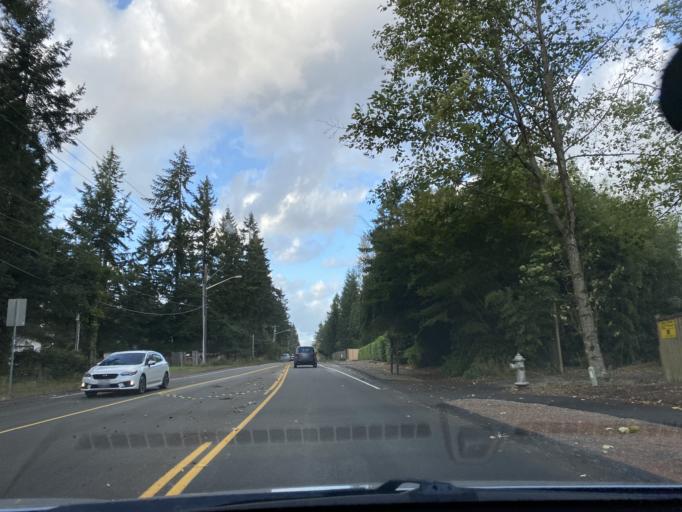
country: US
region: Washington
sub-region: Pierce County
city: South Hill
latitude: 47.1040
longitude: -122.2668
